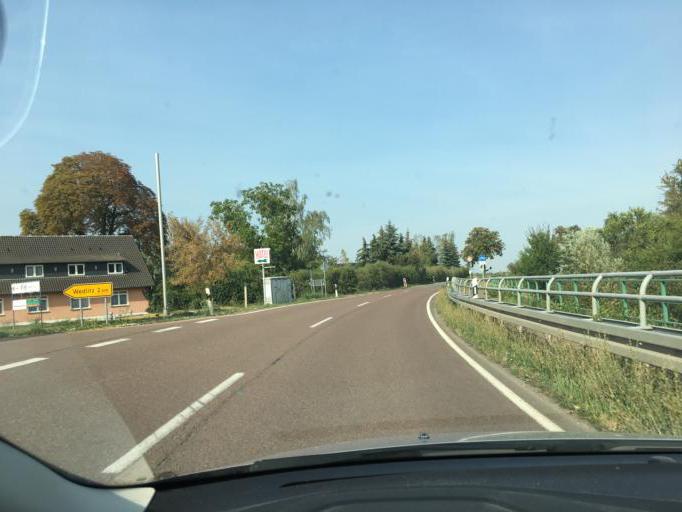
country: DE
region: Saxony-Anhalt
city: Nienburg/Saale
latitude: 51.8443
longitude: 11.7788
